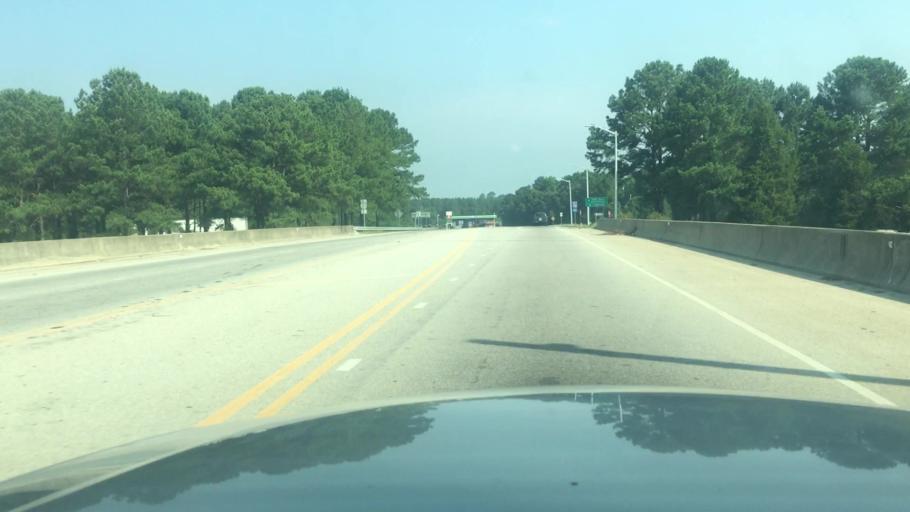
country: US
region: North Carolina
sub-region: Cumberland County
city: Hope Mills
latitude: 34.9380
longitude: -78.9225
